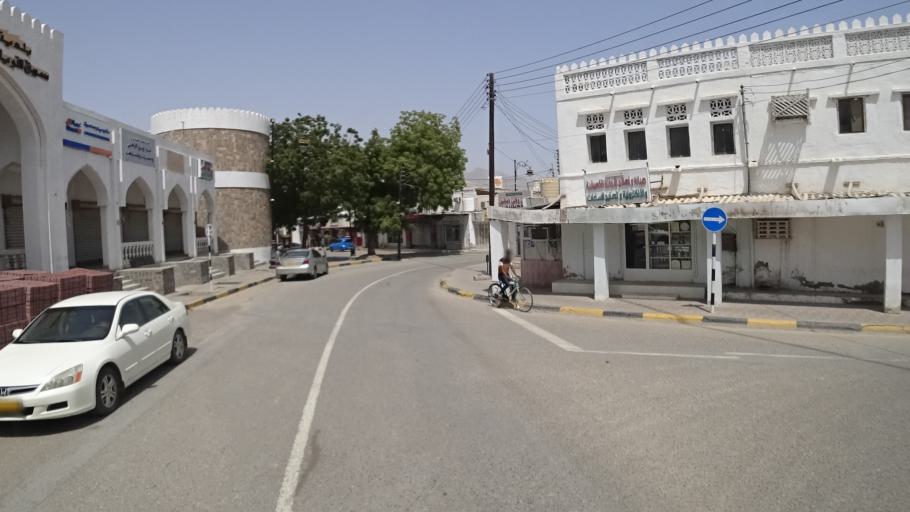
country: OM
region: Muhafazat Masqat
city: Muscat
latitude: 23.2641
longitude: 58.9159
